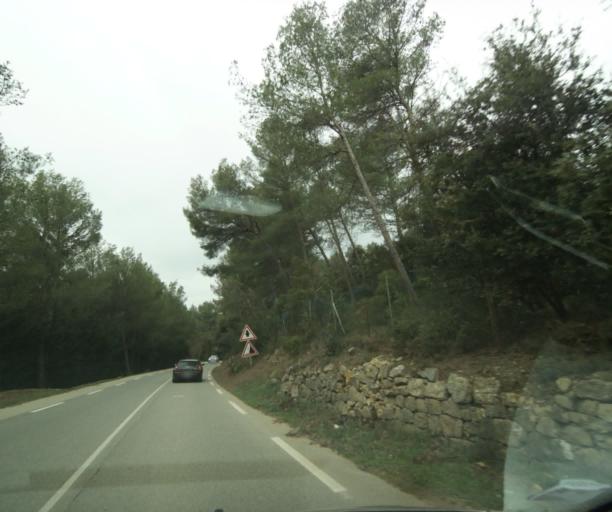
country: FR
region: Provence-Alpes-Cote d'Azur
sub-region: Departement des Bouches-du-Rhone
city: Saint-Marc-Jaumegarde
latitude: 43.5434
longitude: 5.5102
